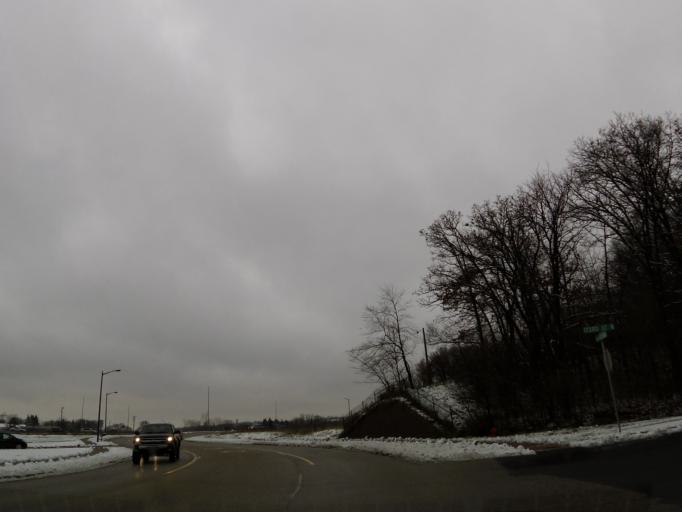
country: US
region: Minnesota
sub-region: Dakota County
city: Lakeville
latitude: 44.6981
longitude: -93.2855
